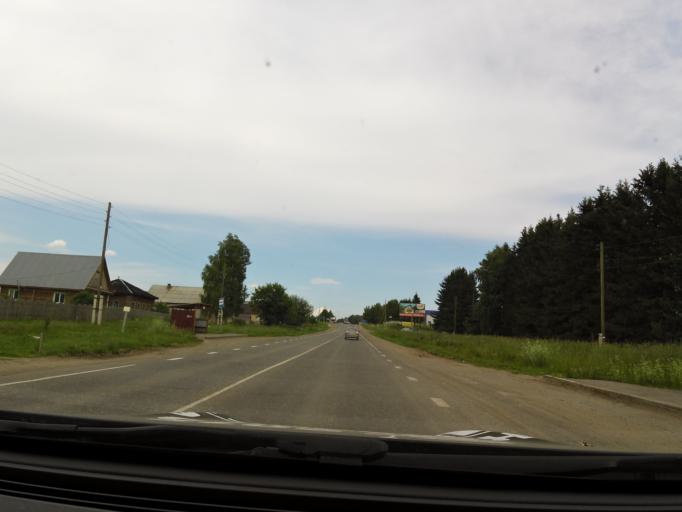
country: RU
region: Kirov
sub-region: Kirovo-Chepetskiy Rayon
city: Kirov
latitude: 58.6323
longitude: 49.8212
